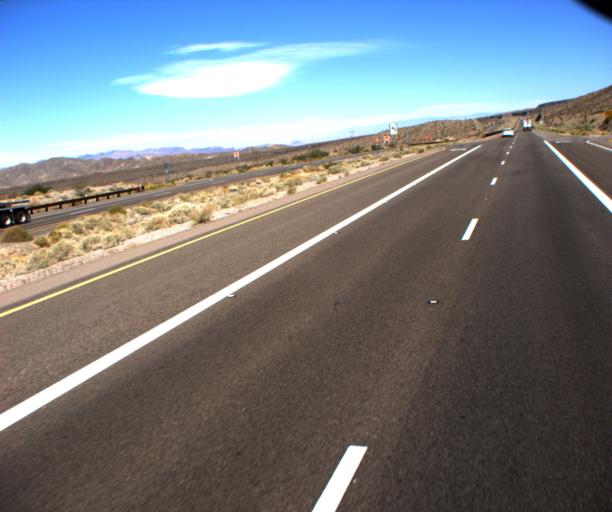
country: US
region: Nevada
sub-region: Clark County
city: Boulder City
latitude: 35.9344
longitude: -114.6371
